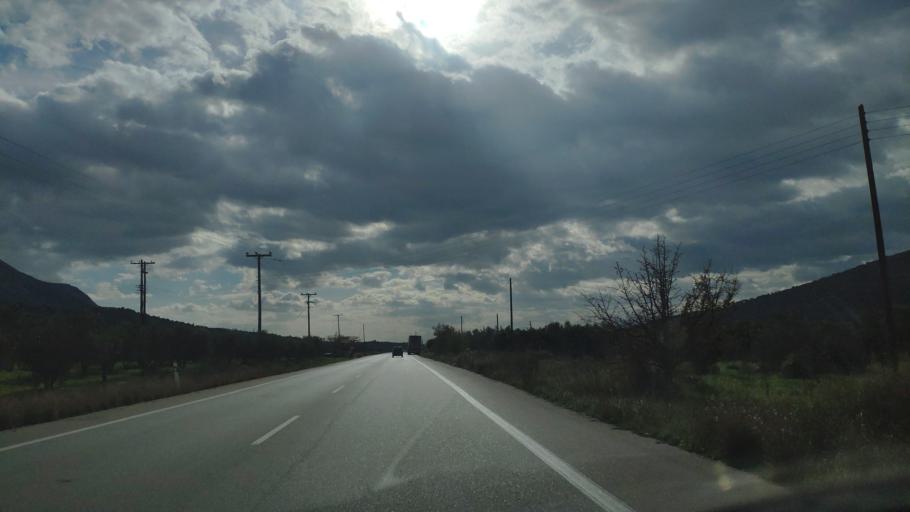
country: GR
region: Peloponnese
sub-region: Nomos Argolidos
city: Koutsopodi
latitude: 37.7483
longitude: 22.7359
